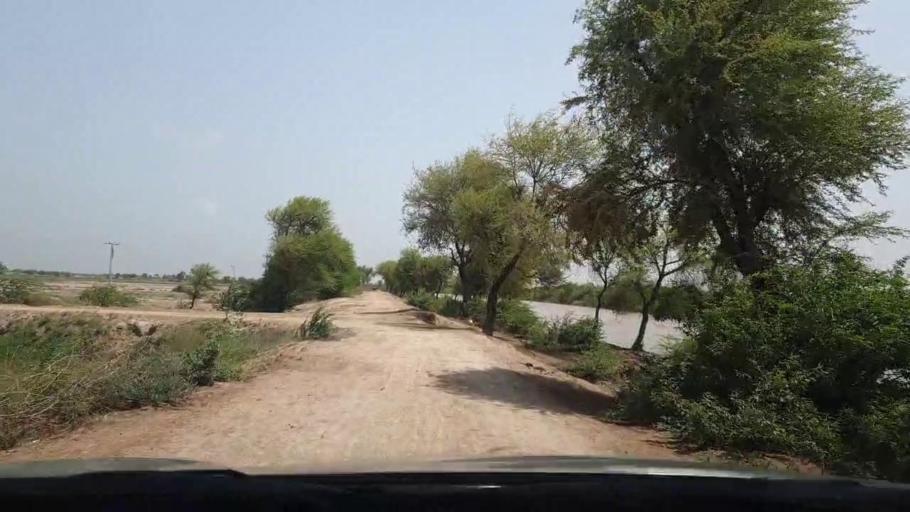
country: PK
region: Sindh
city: Talhar
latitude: 24.9223
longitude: 68.8398
